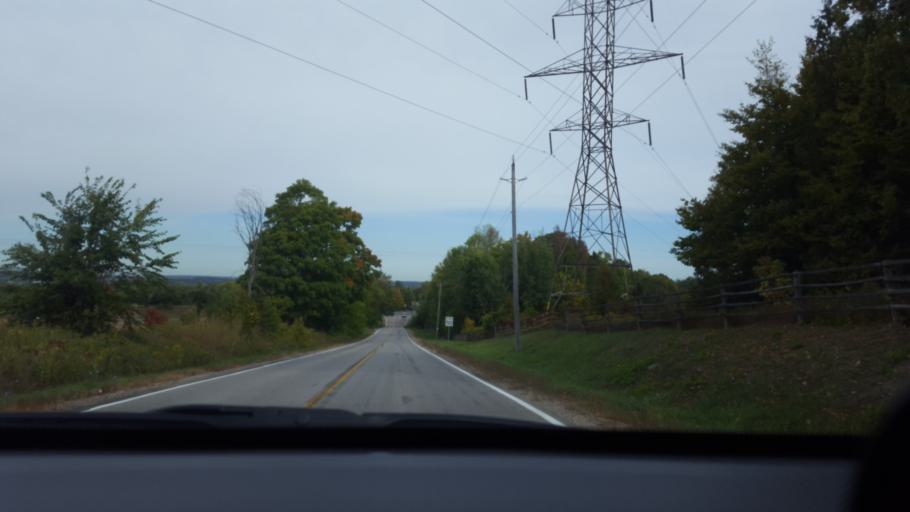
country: CA
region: Ontario
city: Newmarket
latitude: 44.0344
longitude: -79.5556
